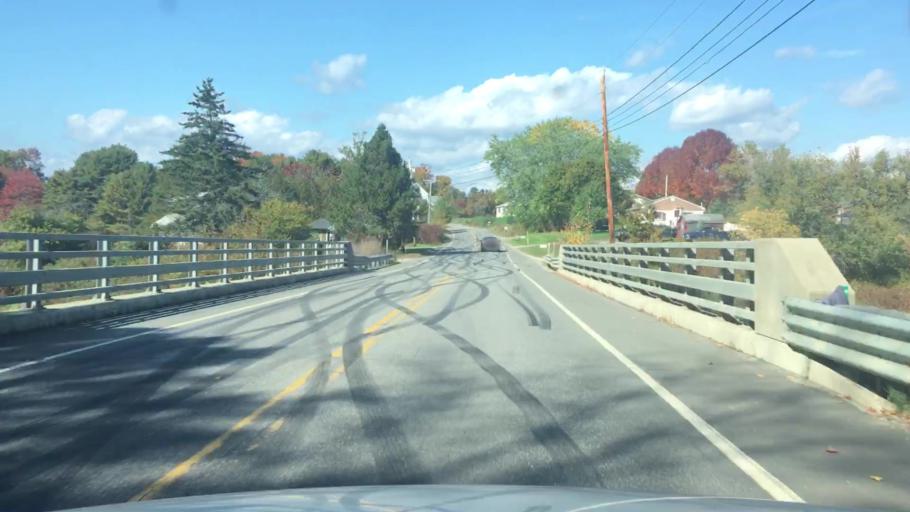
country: US
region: Maine
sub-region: Knox County
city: Thomaston
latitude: 44.0839
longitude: -69.2093
